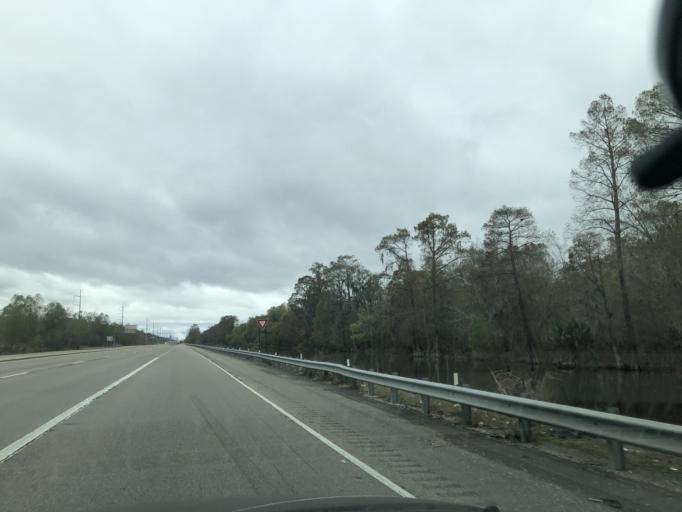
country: US
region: Louisiana
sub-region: Saint Charles Parish
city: Saint Rose
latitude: 29.9772
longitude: -90.3255
